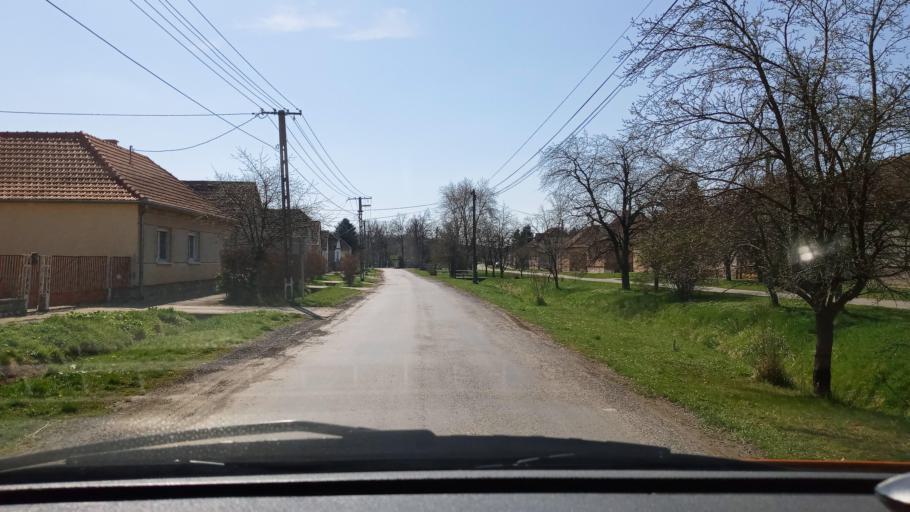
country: HU
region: Baranya
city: Pecsvarad
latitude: 46.0606
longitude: 18.4510
